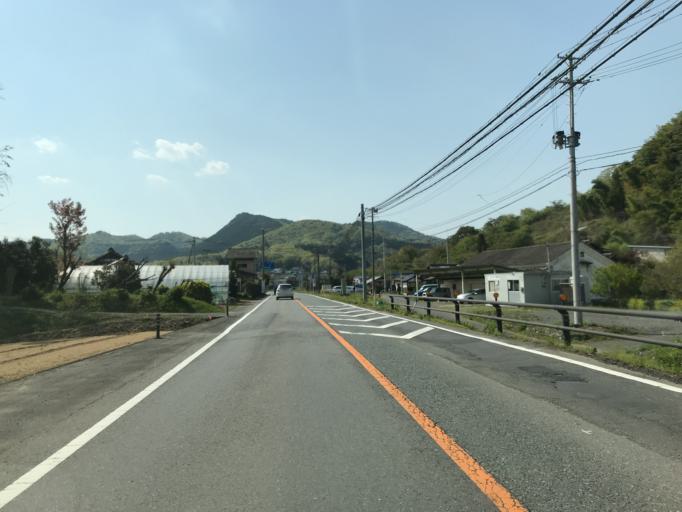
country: JP
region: Fukushima
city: Iwaki
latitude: 36.9539
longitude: 140.7587
